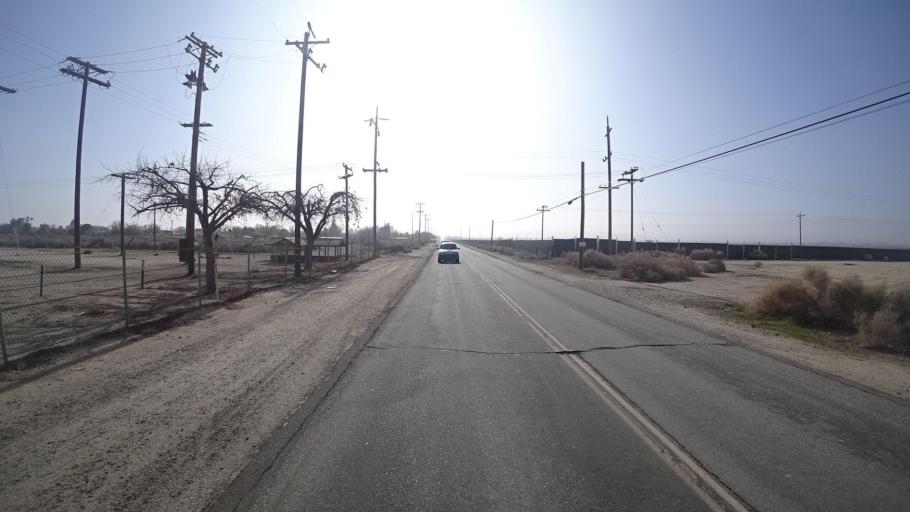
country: US
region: California
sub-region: Kern County
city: Ford City
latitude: 35.1660
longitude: -119.4651
